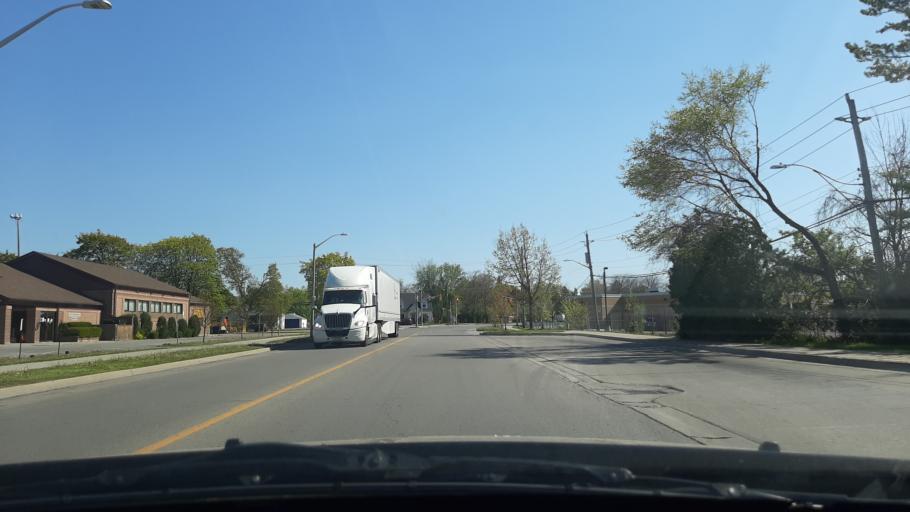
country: CA
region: Ontario
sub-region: Regional Municipality of Niagara
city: St. Catharines
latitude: 43.2138
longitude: -79.2171
